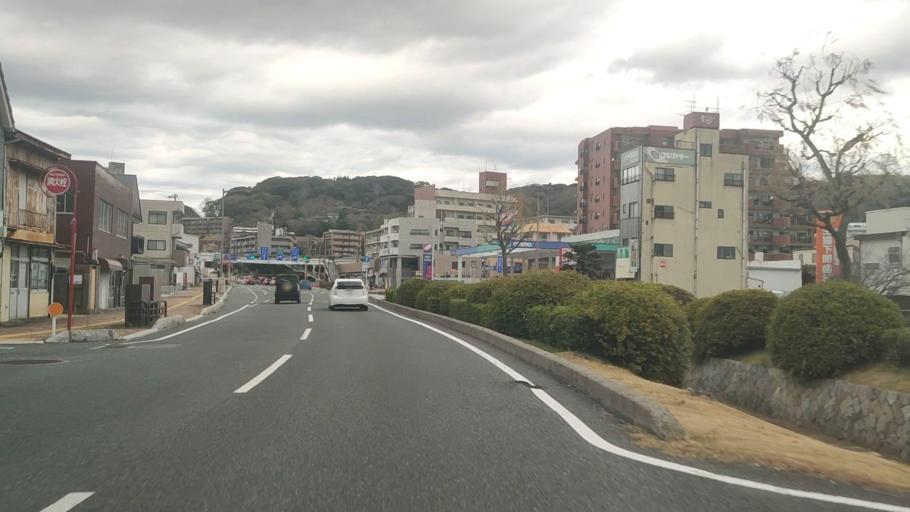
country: JP
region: Yamaguchi
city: Shimonoseki
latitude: 33.9661
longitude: 130.9418
